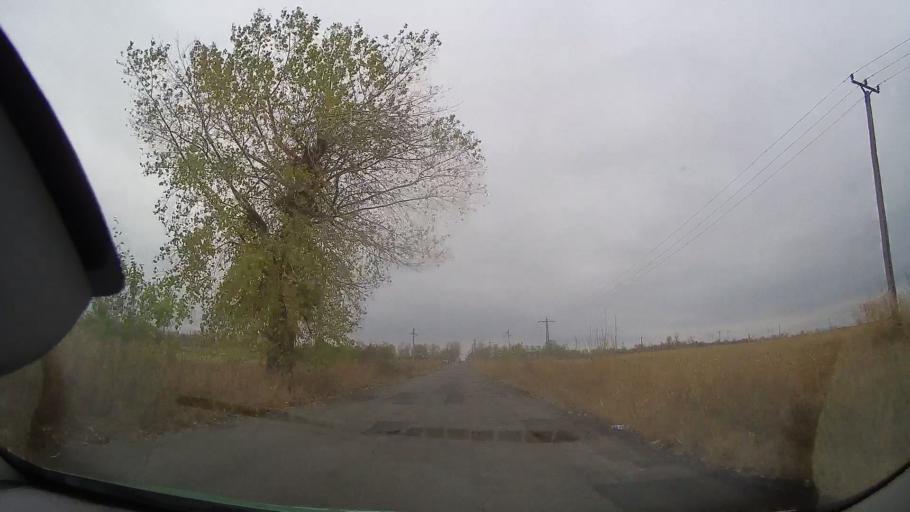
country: RO
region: Braila
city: Dudesti
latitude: 44.9389
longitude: 27.4252
